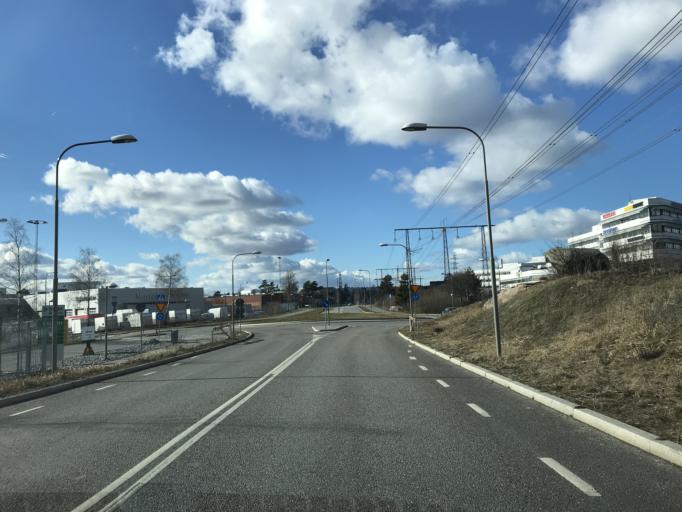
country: SE
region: Stockholm
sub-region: Stockholms Kommun
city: Kista
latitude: 59.4177
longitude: 17.9294
